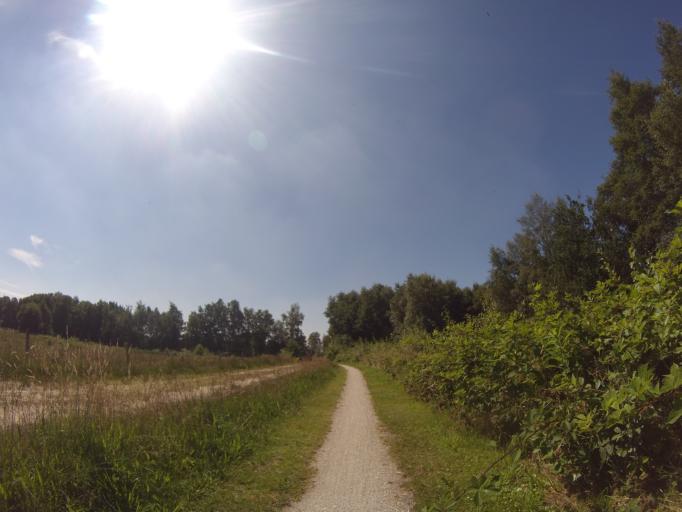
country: DE
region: Lower Saxony
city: Twist
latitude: 52.6708
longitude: 7.0227
